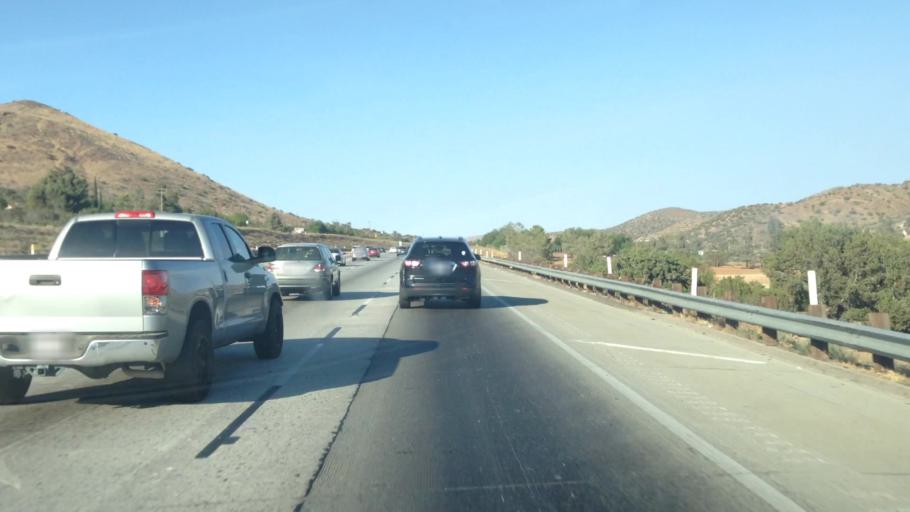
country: US
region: California
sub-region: Los Angeles County
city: Agua Dulce
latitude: 34.4952
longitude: -118.2756
